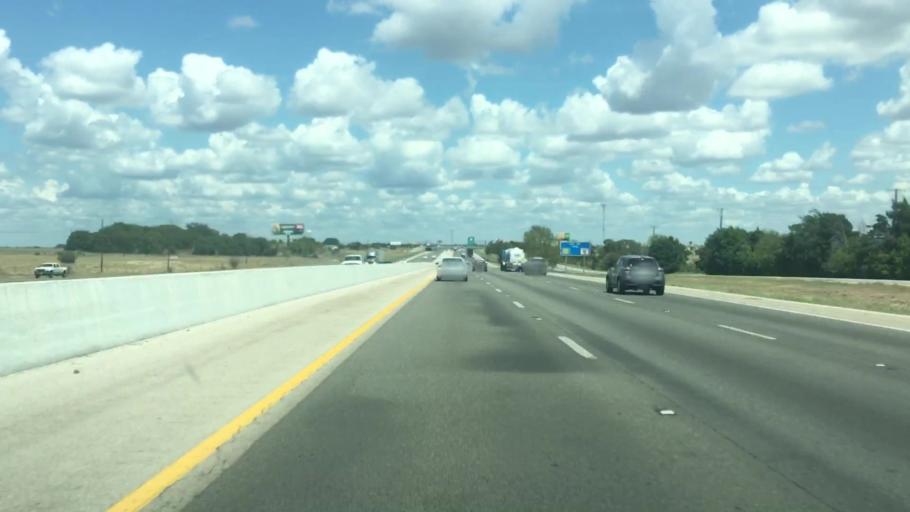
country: US
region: Texas
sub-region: Williamson County
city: Serenada
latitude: 30.7935
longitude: -97.6197
